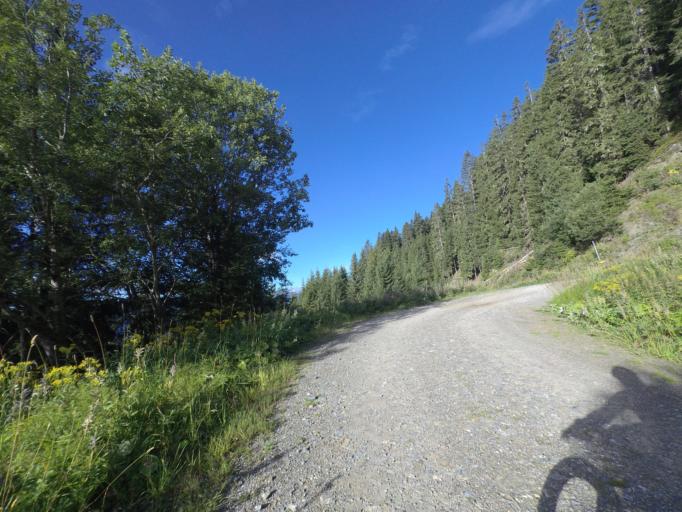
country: AT
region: Salzburg
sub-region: Politischer Bezirk Sankt Johann im Pongau
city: Goldegg
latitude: 47.3476
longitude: 13.0948
